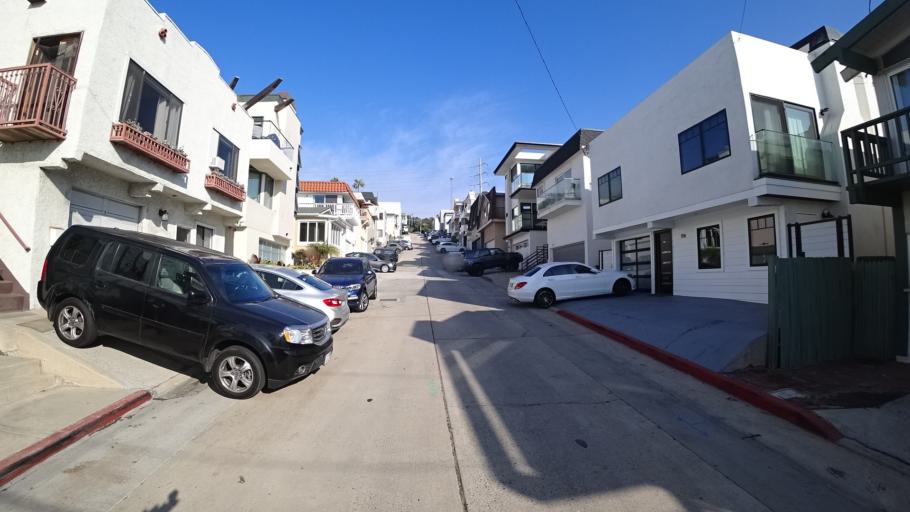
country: US
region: California
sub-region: Los Angeles County
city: El Segundo
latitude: 33.9018
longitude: -118.4197
